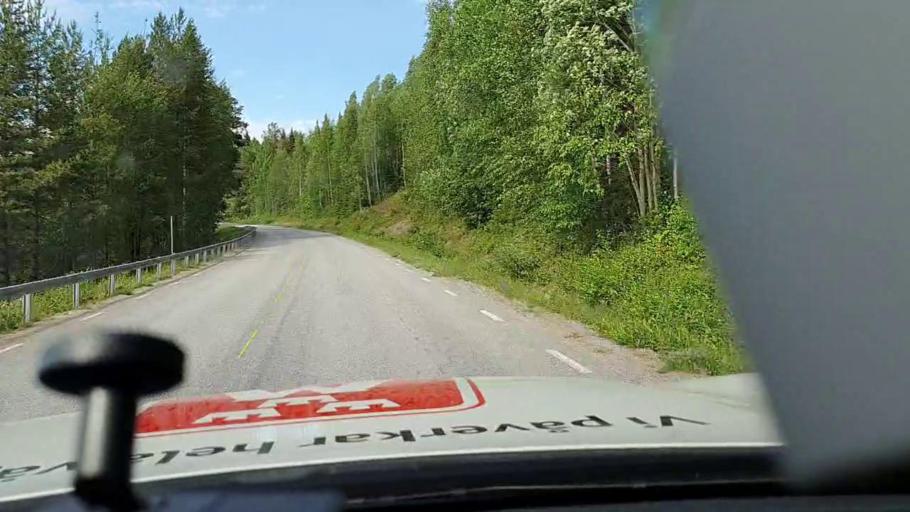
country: SE
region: Norrbotten
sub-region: Gallivare Kommun
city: Gaellivare
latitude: 66.4524
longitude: 20.6567
